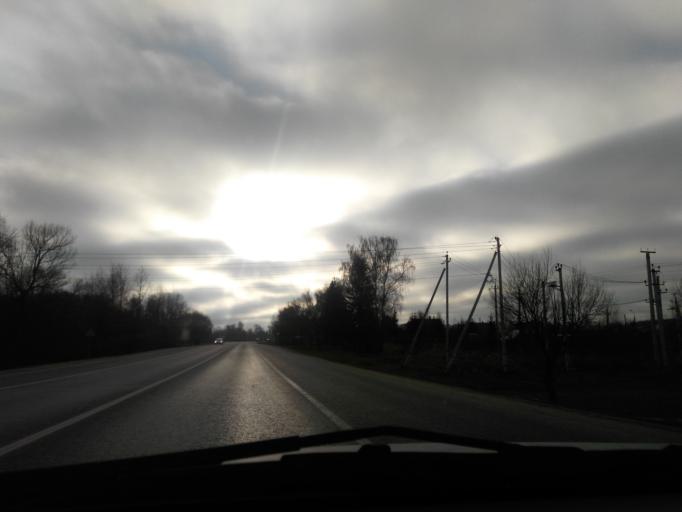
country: RU
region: Moskovskaya
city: Troitsk
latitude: 55.3408
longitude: 37.1725
